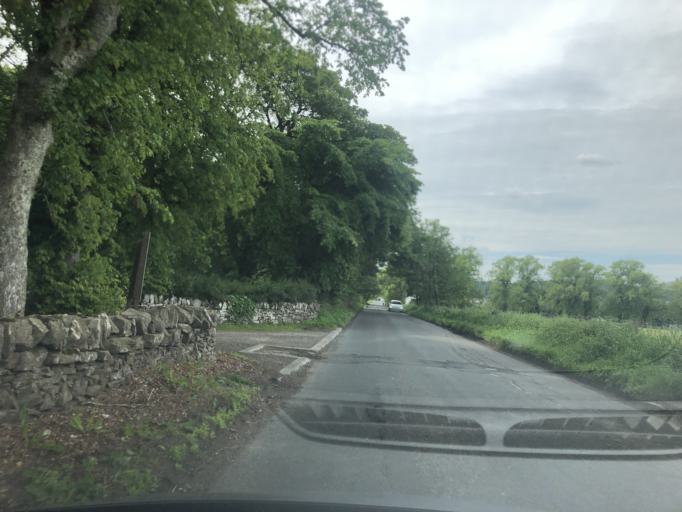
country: GB
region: Scotland
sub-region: The Scottish Borders
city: West Linton
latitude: 55.7428
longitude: -3.3435
